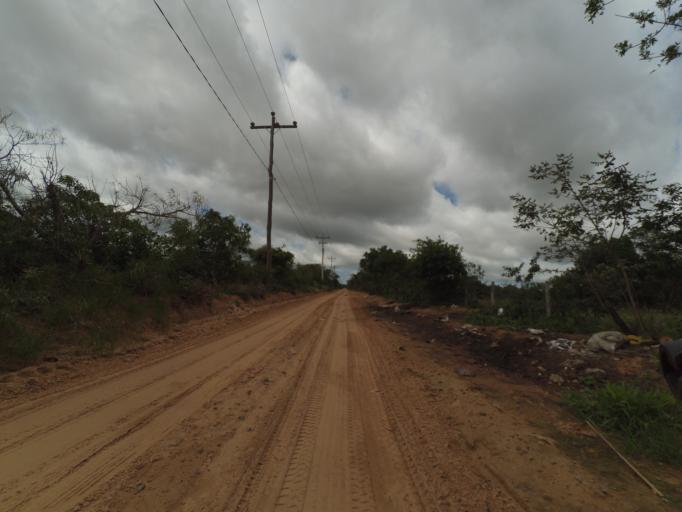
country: BO
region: Santa Cruz
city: Santa Rita
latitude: -17.9077
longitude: -63.2461
